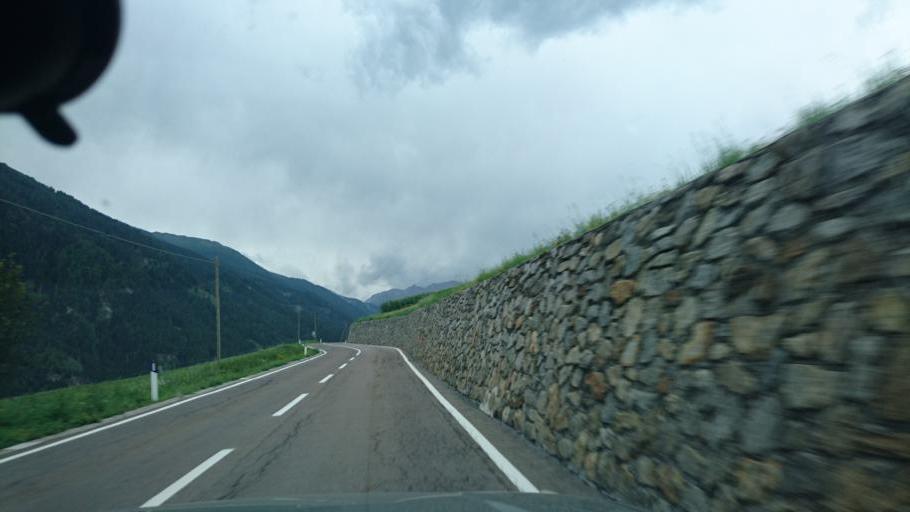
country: IT
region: Trentino-Alto Adige
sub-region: Bolzano
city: Tubre
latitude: 46.6520
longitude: 10.4731
